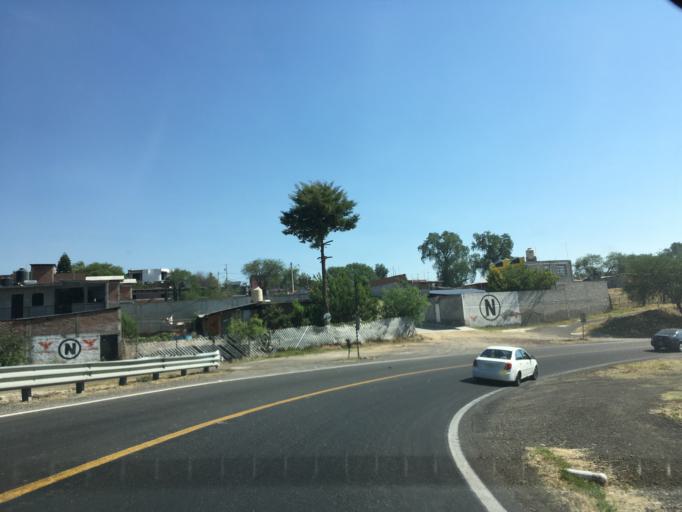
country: MX
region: Michoacan
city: Charo
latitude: 19.7506
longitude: -101.0497
